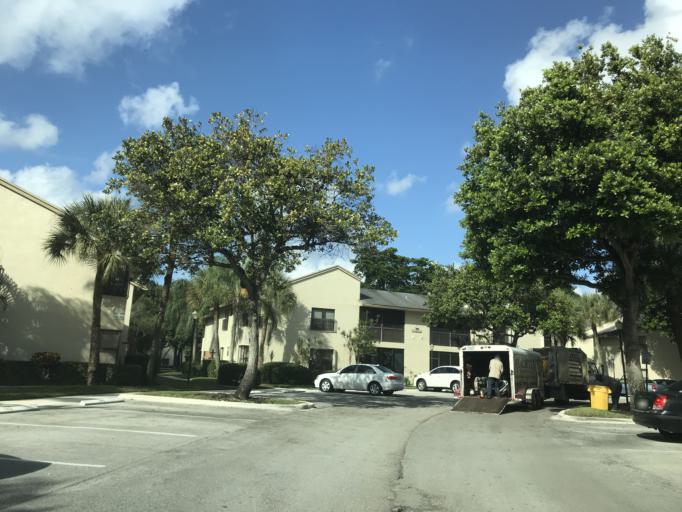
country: US
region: Florida
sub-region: Broward County
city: Coconut Creek
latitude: 26.2558
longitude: -80.1890
